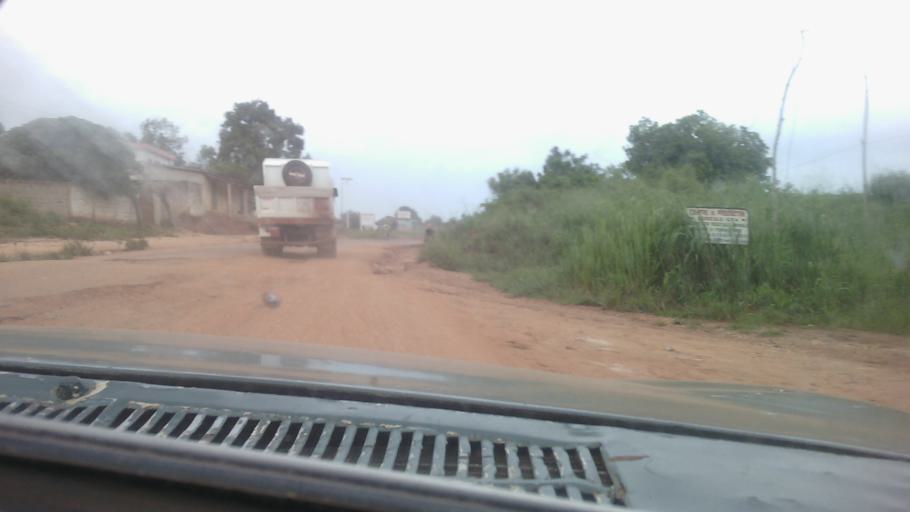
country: BJ
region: Mono
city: Come
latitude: 6.5054
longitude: 1.8337
